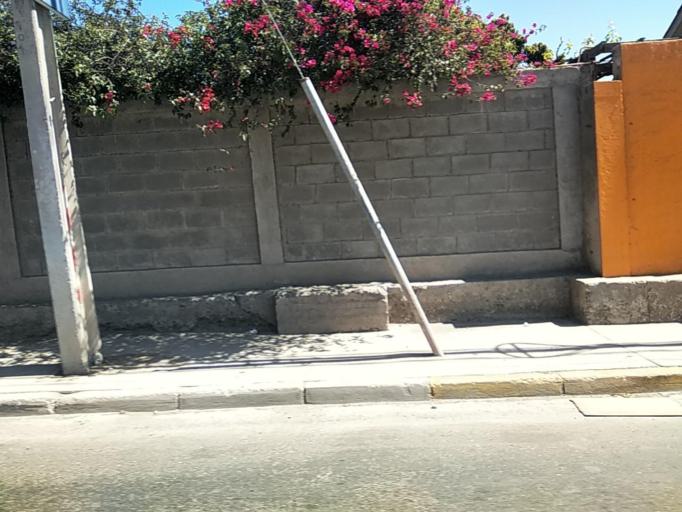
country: CL
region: Atacama
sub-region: Provincia de Copiapo
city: Copiapo
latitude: -27.3978
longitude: -70.2951
